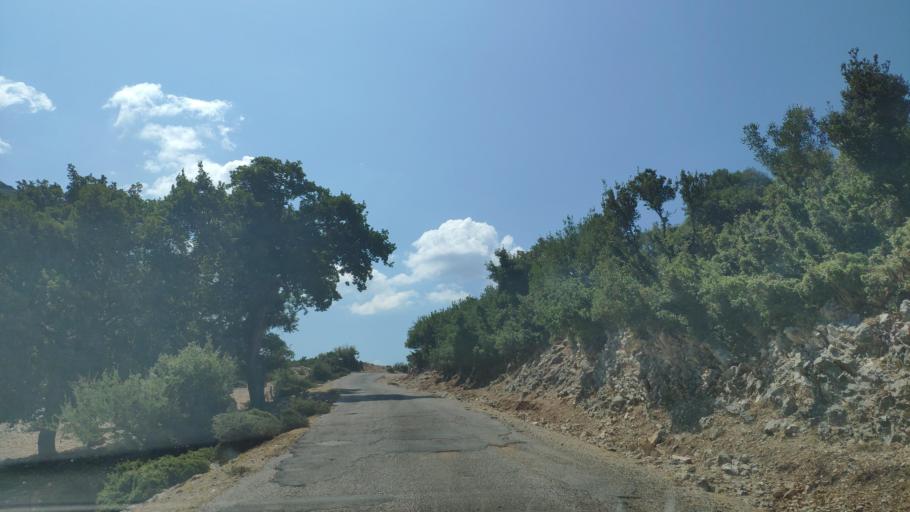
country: GR
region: West Greece
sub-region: Nomos Aitolias kai Akarnanias
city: Monastirakion
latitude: 38.8185
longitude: 20.9337
